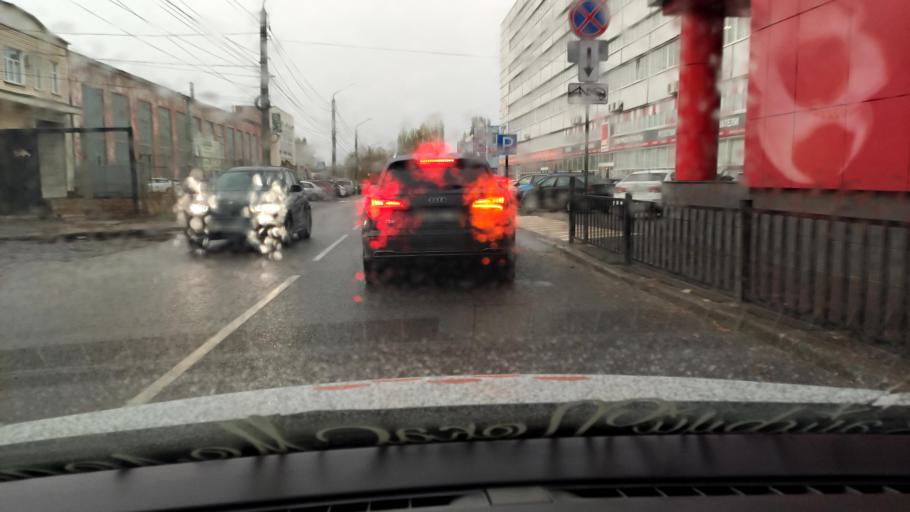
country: RU
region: Voronezj
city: Voronezh
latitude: 51.6808
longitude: 39.1735
